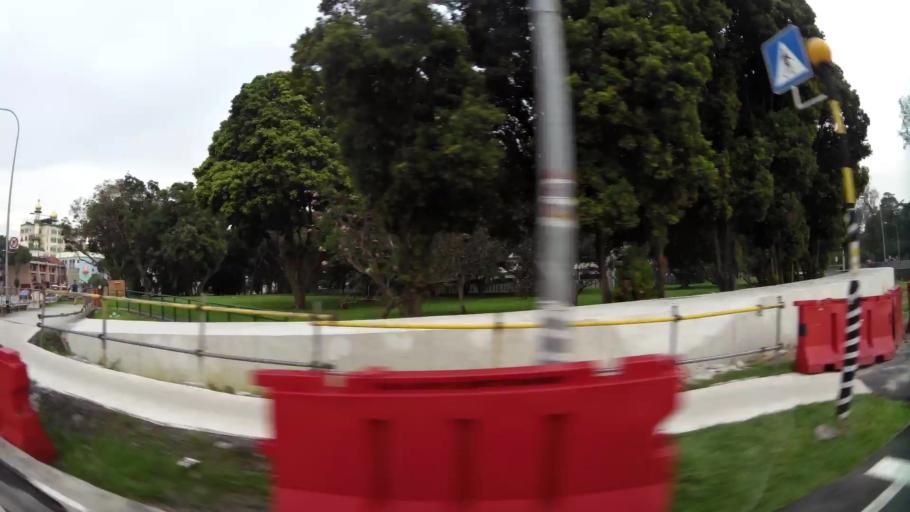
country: SG
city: Singapore
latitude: 1.3084
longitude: 103.8778
